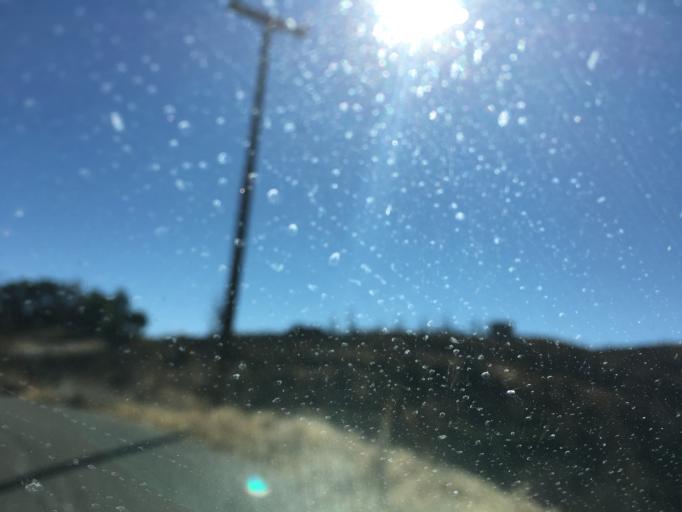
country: US
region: California
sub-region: Los Angeles County
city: Green Valley
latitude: 34.6739
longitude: -118.4517
